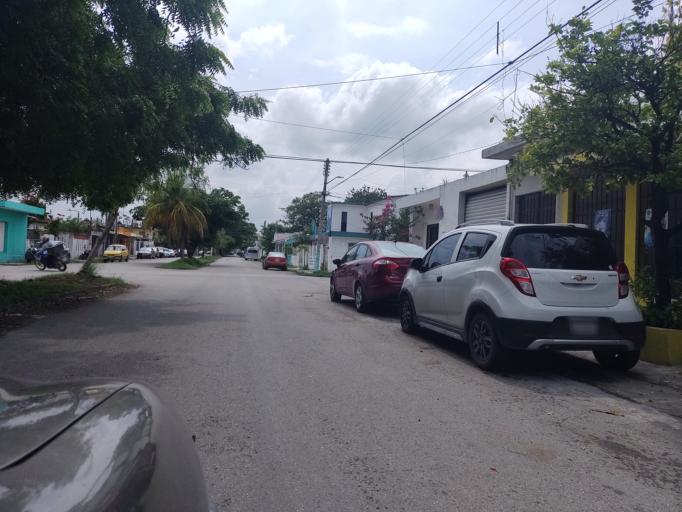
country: MX
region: Quintana Roo
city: Chetumal
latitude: 18.5166
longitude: -88.3094
